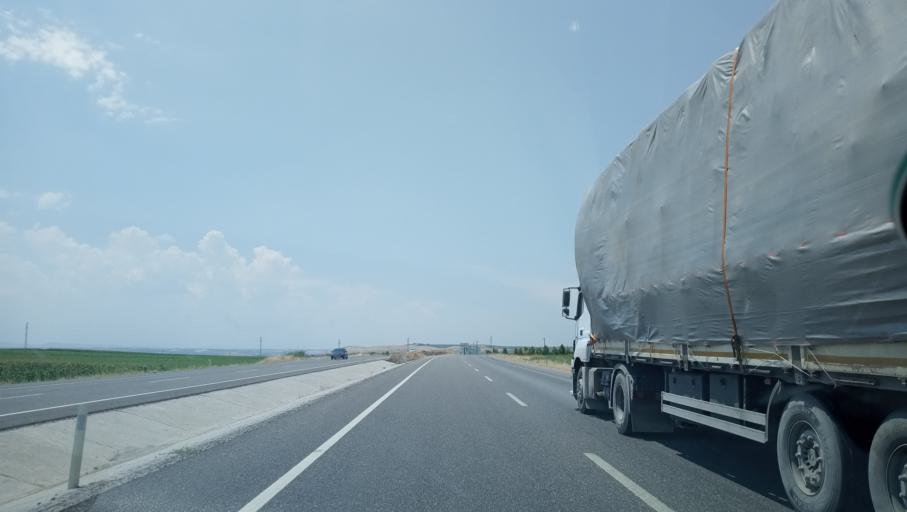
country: TR
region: Diyarbakir
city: Salat
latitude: 37.8541
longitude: 40.8563
